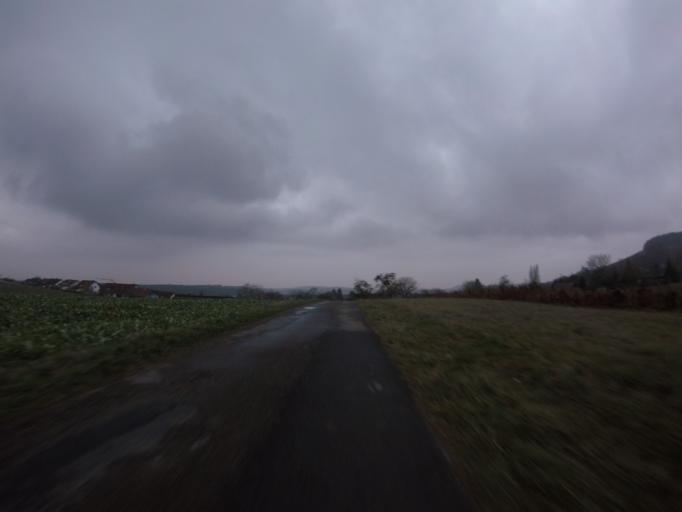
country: DE
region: Baden-Wuerttemberg
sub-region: Regierungsbezirk Stuttgart
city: Aspach
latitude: 48.9957
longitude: 9.3986
